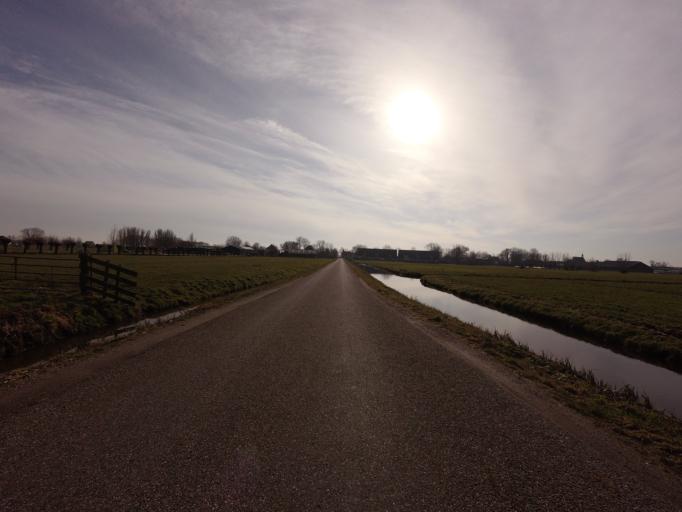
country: NL
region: South Holland
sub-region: Gemeente Sliedrecht
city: Sliedrecht
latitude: 51.8480
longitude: 4.7679
